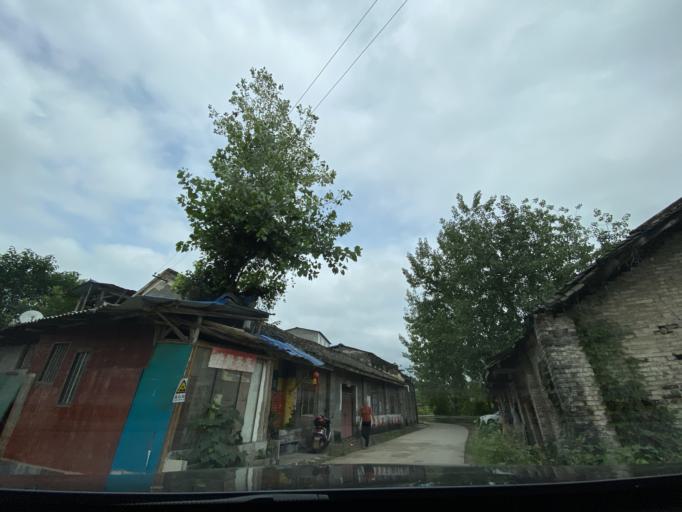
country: CN
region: Sichuan
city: Jiancheng
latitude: 30.3992
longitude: 104.5662
